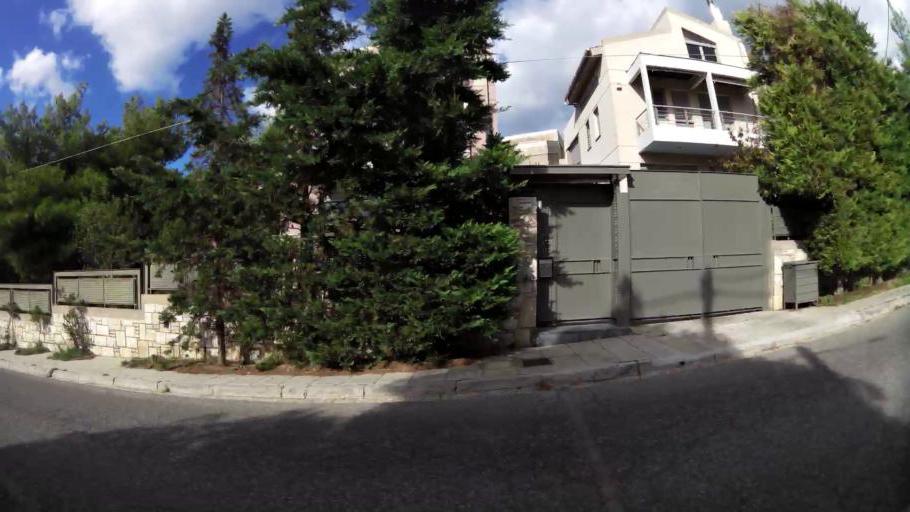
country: GR
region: Attica
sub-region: Nomarchia Anatolikis Attikis
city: Thrakomakedones
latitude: 38.1231
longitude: 23.7559
